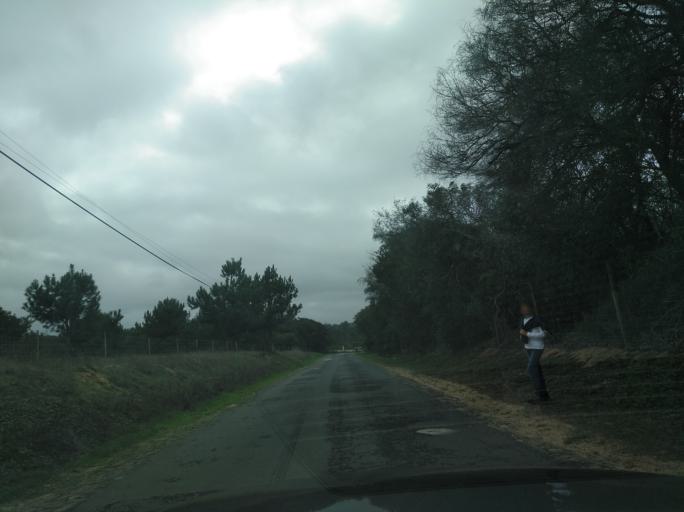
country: PT
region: Setubal
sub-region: Sines
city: Porto Covo
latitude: 37.8334
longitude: -8.7870
